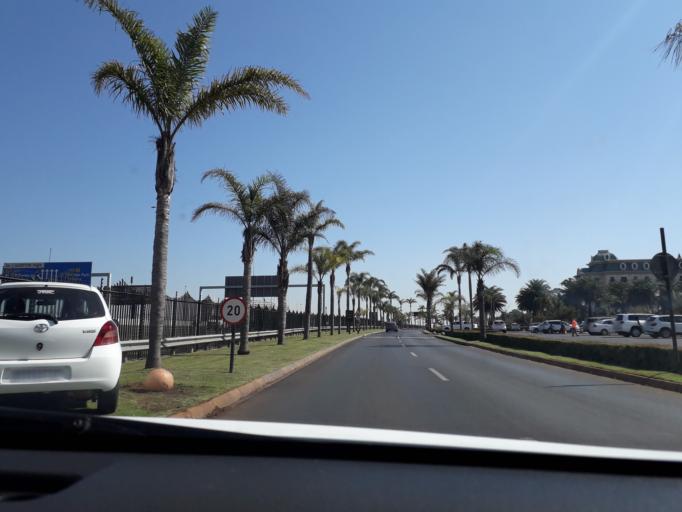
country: ZA
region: Gauteng
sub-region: Ekurhuleni Metropolitan Municipality
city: Boksburg
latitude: -26.1462
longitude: 28.2202
